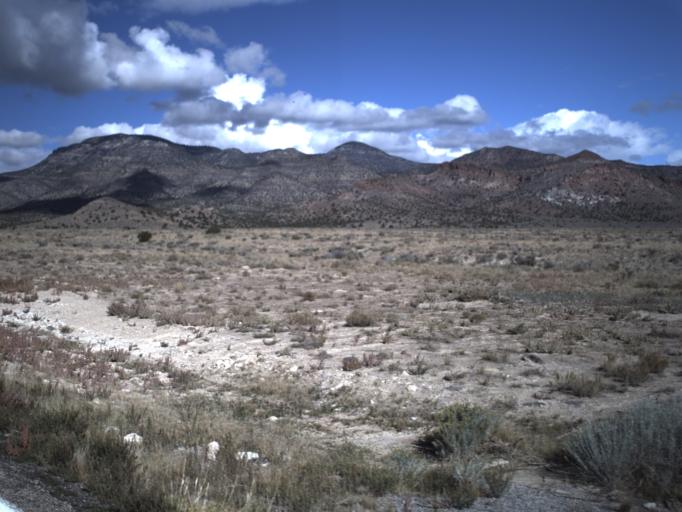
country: US
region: Utah
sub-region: Beaver County
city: Milford
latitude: 38.4971
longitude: -113.4886
